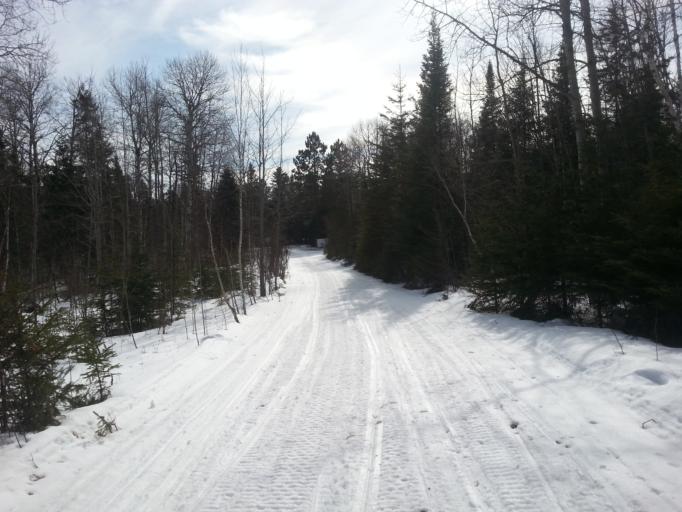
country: CA
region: Ontario
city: Greater Sudbury
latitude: 46.3447
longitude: -80.9019
